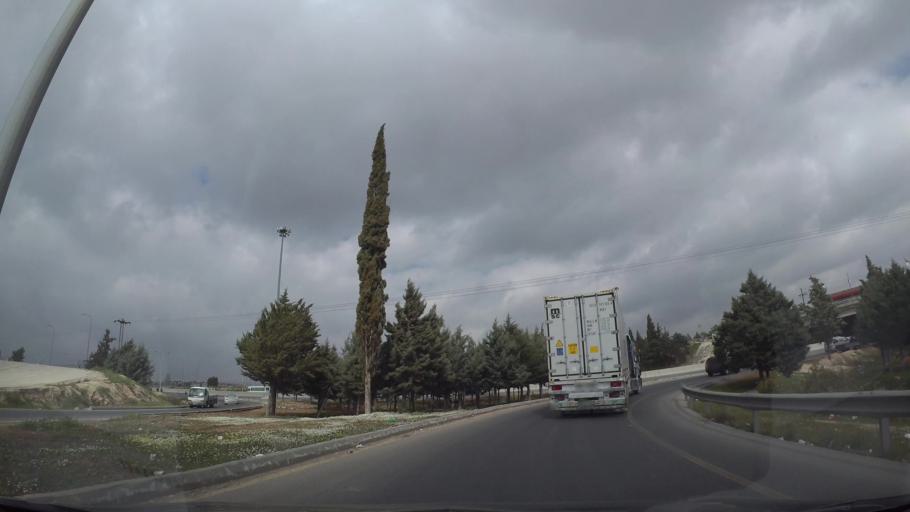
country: JO
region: Amman
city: Jawa
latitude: 31.8136
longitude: 35.9073
